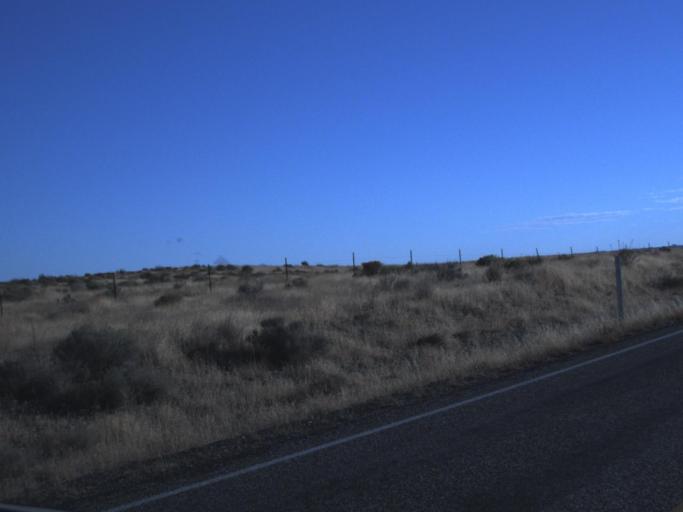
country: US
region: Washington
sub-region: Benton County
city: West Richland
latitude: 46.3823
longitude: -119.4299
